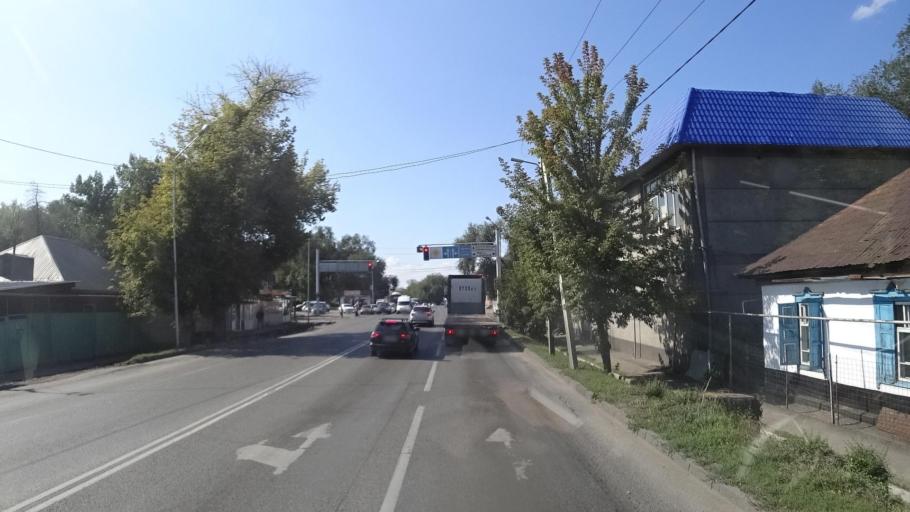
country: KZ
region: Almaty Oblysy
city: Pervomayskiy
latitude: 43.3545
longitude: 76.9498
